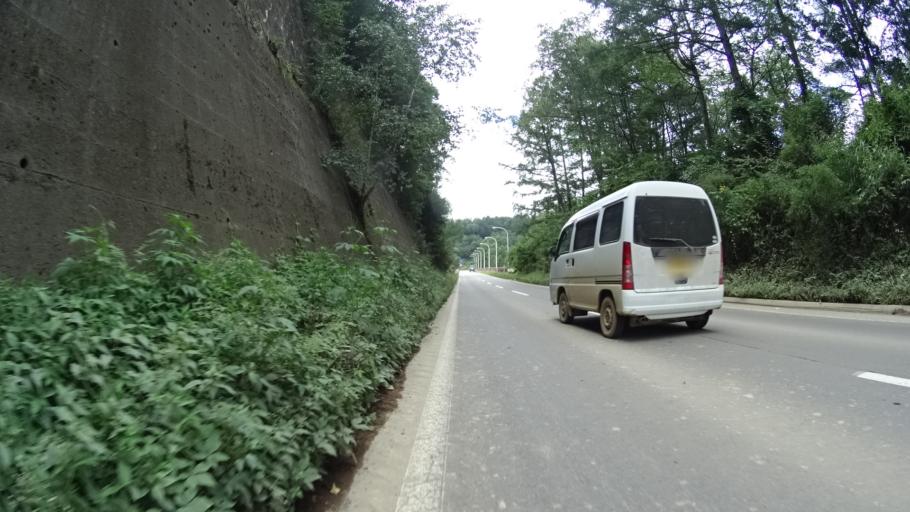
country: JP
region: Nagano
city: Saku
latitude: 35.9623
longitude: 138.5402
